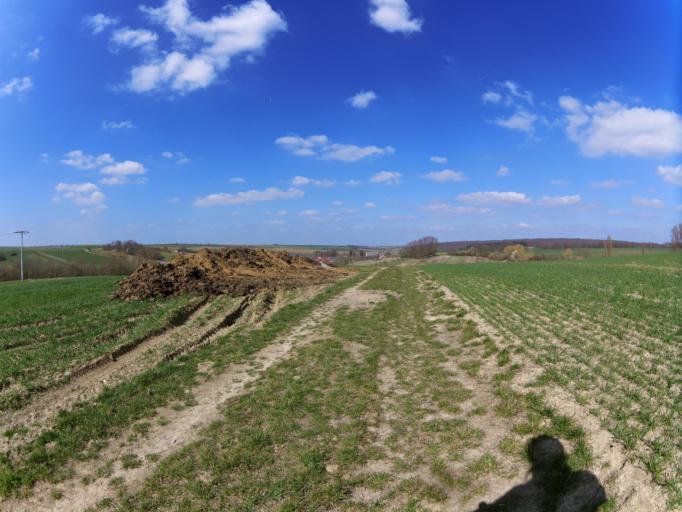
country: DE
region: Bavaria
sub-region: Regierungsbezirk Unterfranken
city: Dettelbach
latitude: 49.8356
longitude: 10.1517
